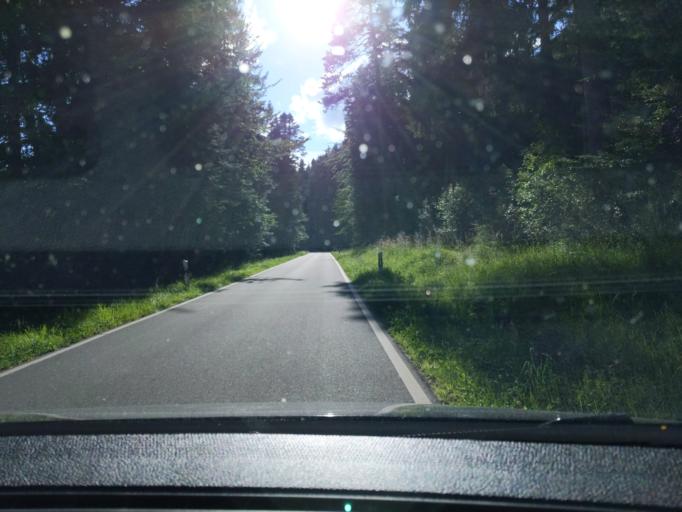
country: DE
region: Baden-Wuerttemberg
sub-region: Karlsruhe Region
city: Glatten
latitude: 48.3965
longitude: 8.4953
